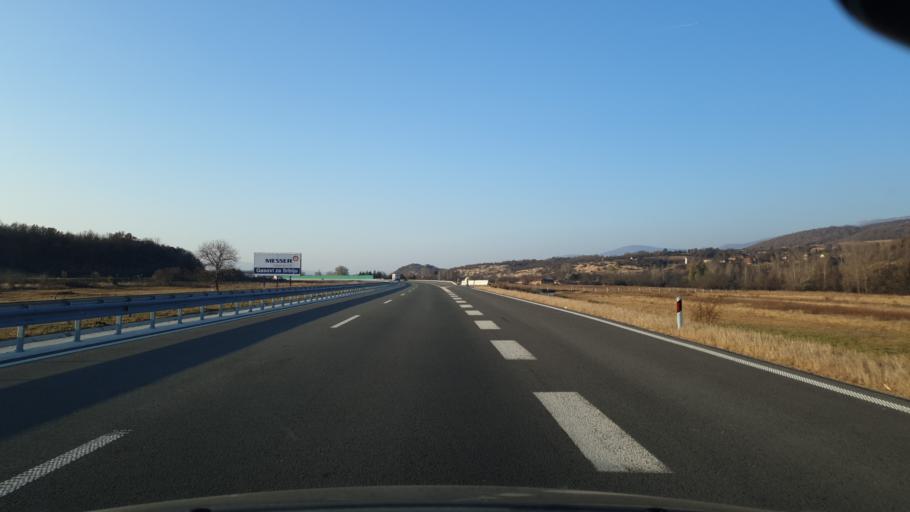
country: RS
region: Central Serbia
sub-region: Pirotski Okrug
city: Dimitrovgrad
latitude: 43.0534
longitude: 22.6981
